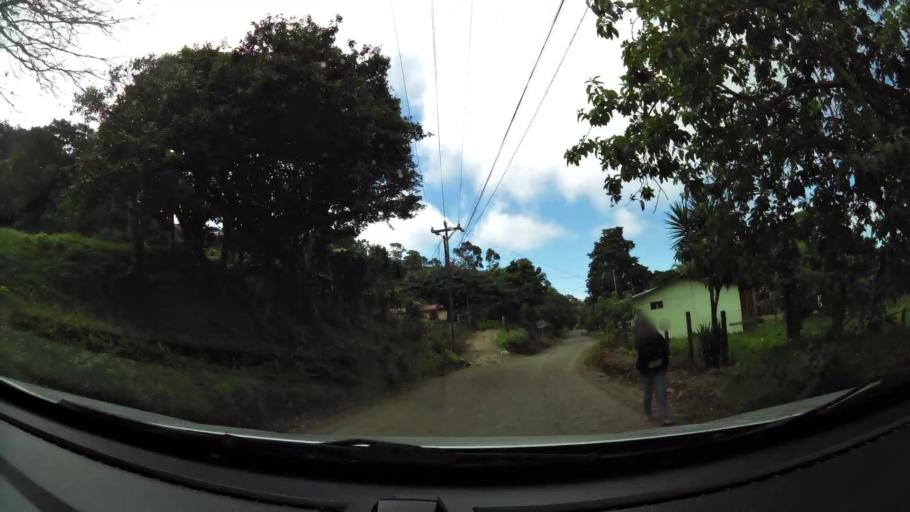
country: CR
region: Guanacaste
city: Juntas
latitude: 10.3498
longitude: -84.9102
